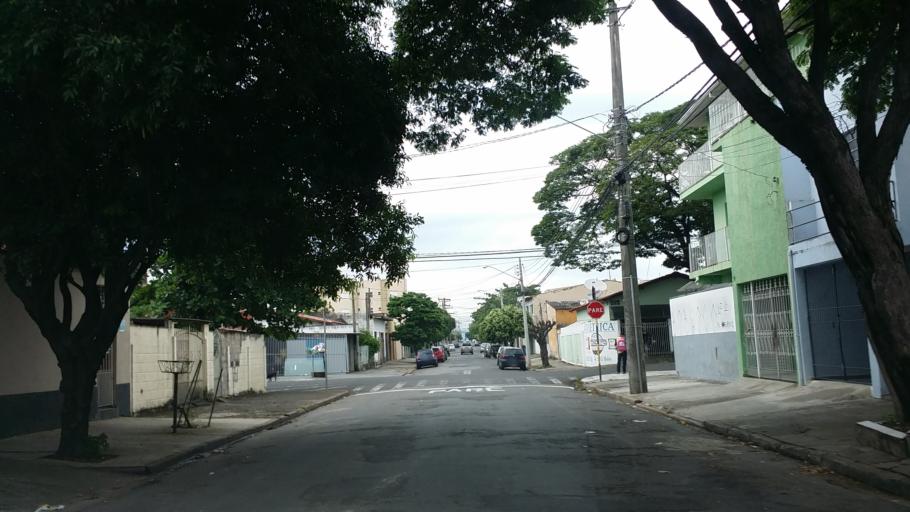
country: BR
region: Sao Paulo
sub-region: Indaiatuba
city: Indaiatuba
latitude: -23.1068
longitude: -47.2179
